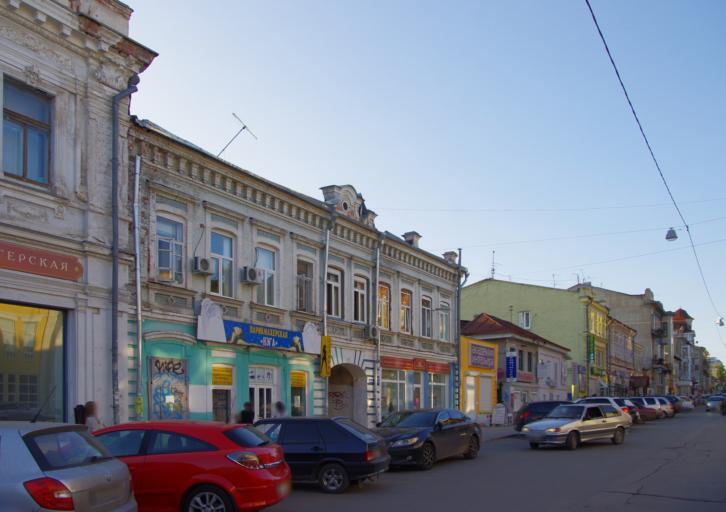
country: RU
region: Samara
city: Samara
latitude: 53.1869
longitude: 50.0965
